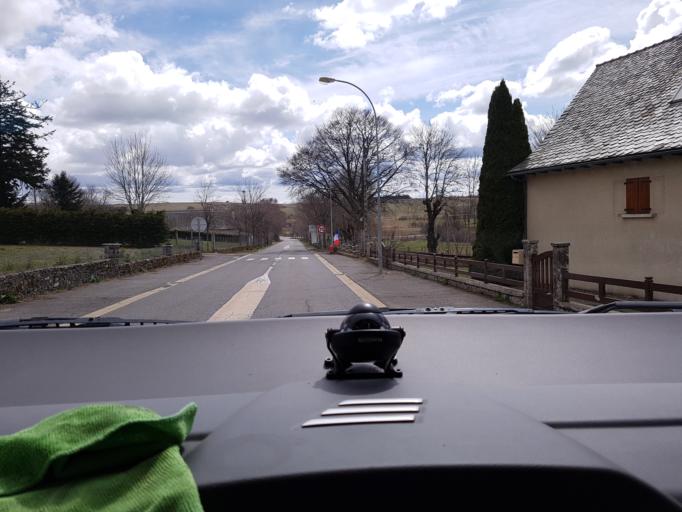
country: FR
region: Midi-Pyrenees
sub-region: Departement de l'Aveyron
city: Laguiole
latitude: 44.7682
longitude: 2.8826
